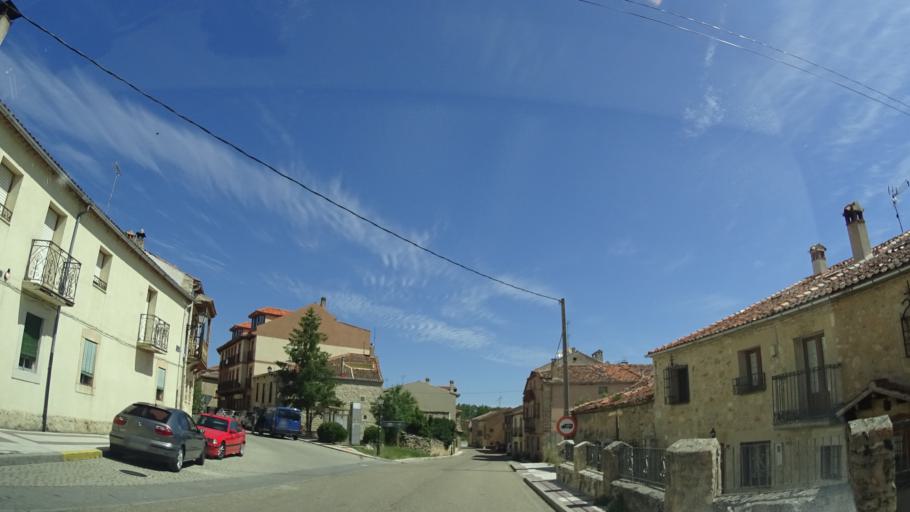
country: ES
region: Castille and Leon
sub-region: Provincia de Segovia
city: Pradena
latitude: 41.1378
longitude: -3.6878
